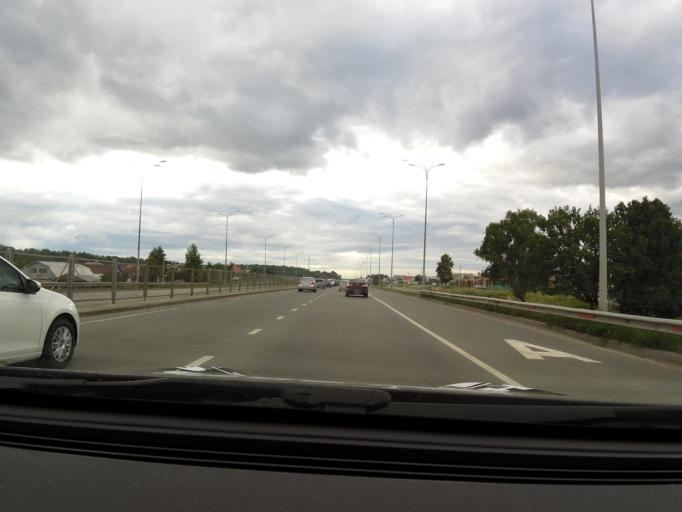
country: RU
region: Tatarstan
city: Osinovo
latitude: 55.8522
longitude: 48.8837
